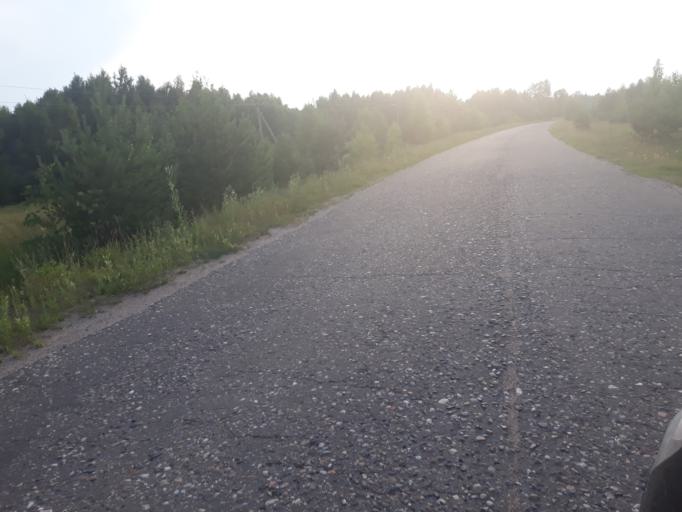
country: RU
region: Jaroslavl
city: Petrovsk
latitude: 56.8746
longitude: 39.0842
